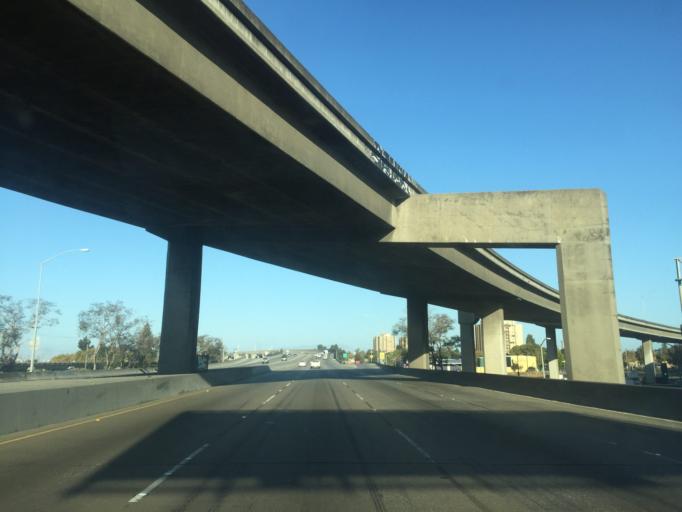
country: US
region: California
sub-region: Alameda County
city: Oakland
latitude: 37.8002
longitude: -122.2789
